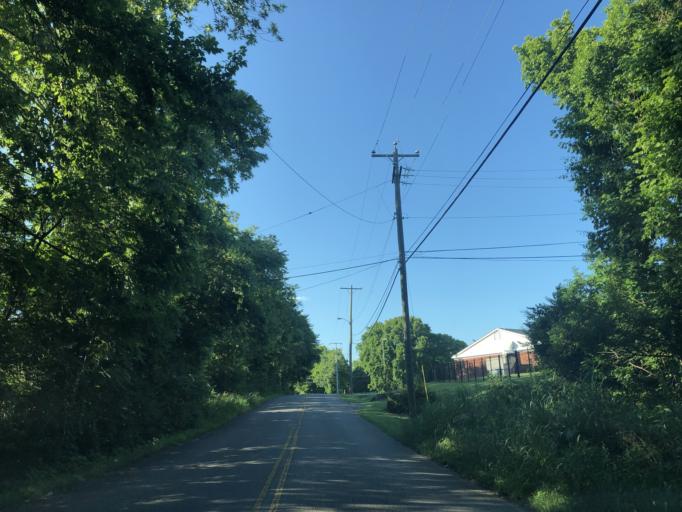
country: US
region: Tennessee
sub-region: Davidson County
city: Nashville
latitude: 36.2066
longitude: -86.8608
